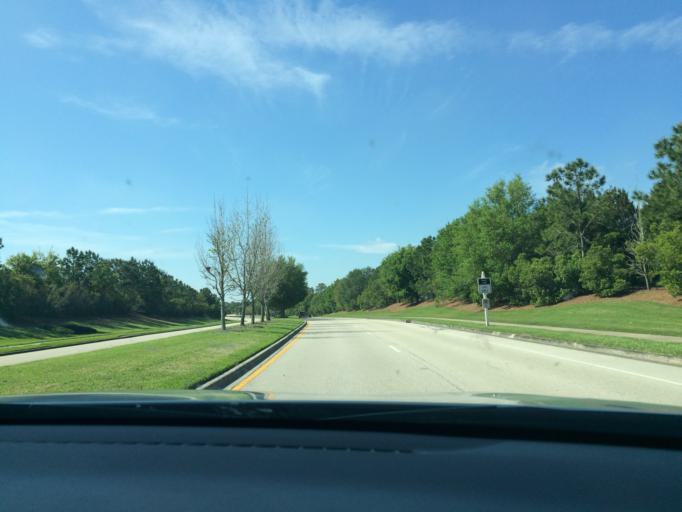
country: US
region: Florida
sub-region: Sarasota County
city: The Meadows
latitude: 27.4222
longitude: -82.3984
